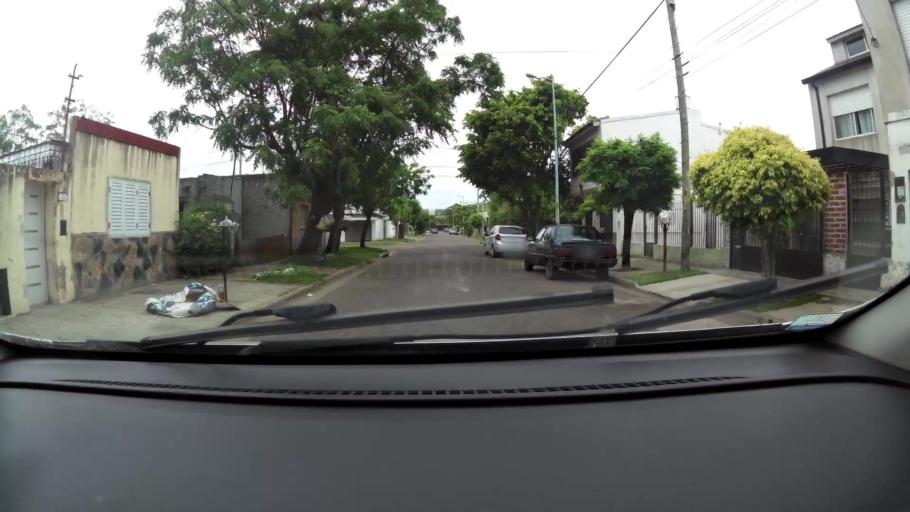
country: AR
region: Buenos Aires
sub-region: Partido de Zarate
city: Zarate
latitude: -34.0940
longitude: -59.0362
